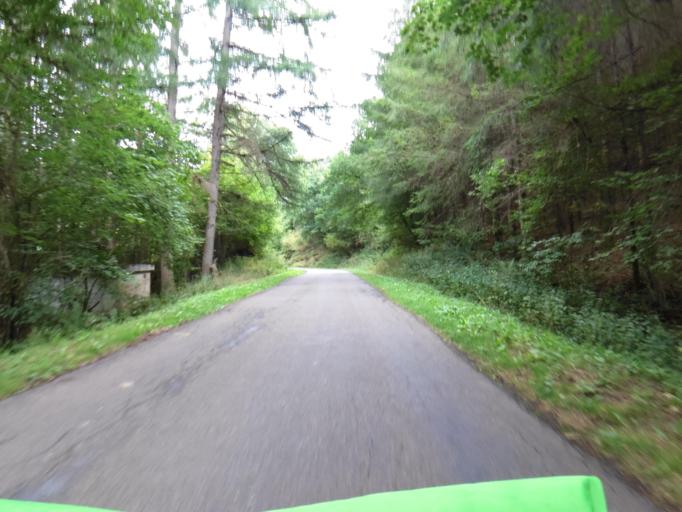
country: BE
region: Wallonia
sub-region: Province de Namur
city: Bievre
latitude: 49.8959
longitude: 5.0016
